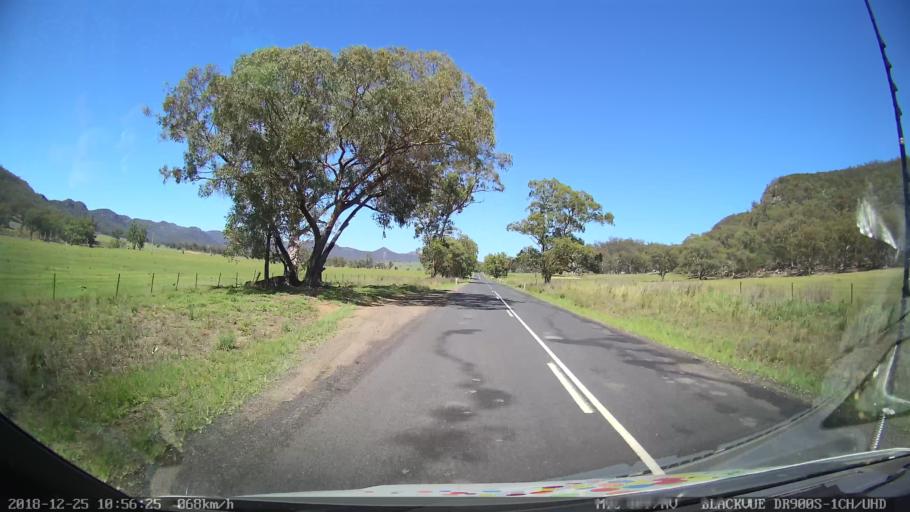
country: AU
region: New South Wales
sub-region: Upper Hunter Shire
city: Merriwa
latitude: -32.4012
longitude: 150.2628
